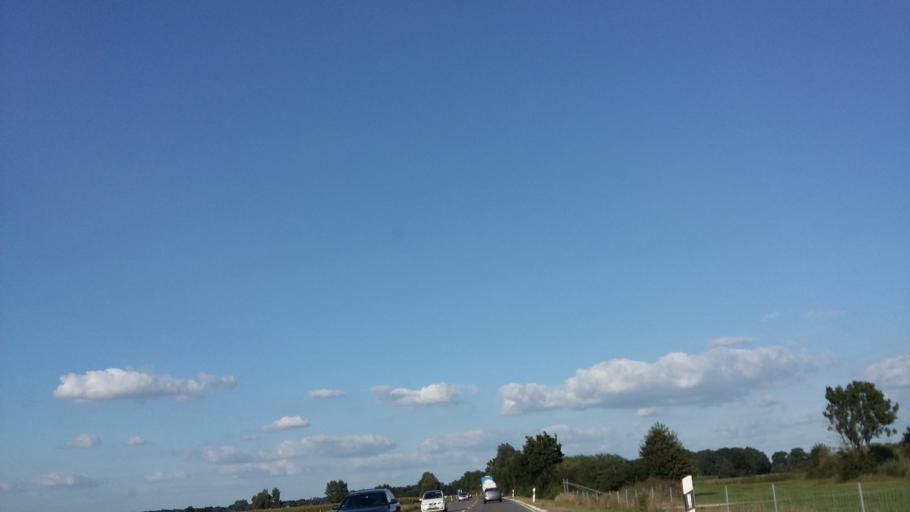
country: DE
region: Bavaria
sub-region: Swabia
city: Holzheim
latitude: 48.3976
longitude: 10.0661
